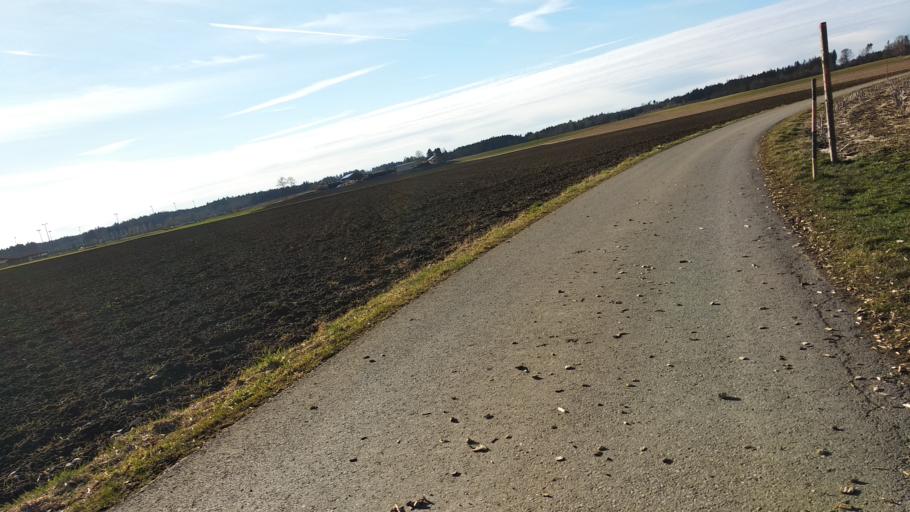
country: DE
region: Bavaria
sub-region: Upper Bavaria
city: Aying
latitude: 47.9773
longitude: 11.7747
